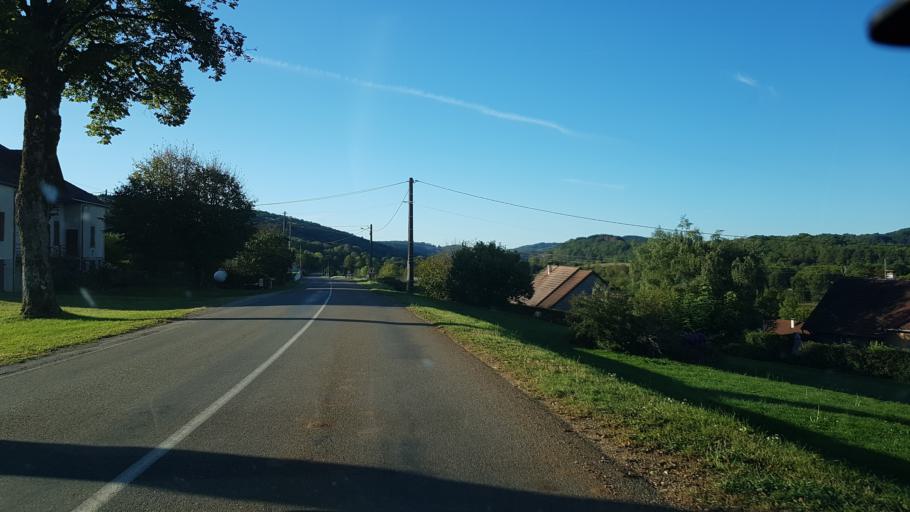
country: FR
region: Franche-Comte
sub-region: Departement du Jura
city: Lons-le-Saunier
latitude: 46.5990
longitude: 5.5197
